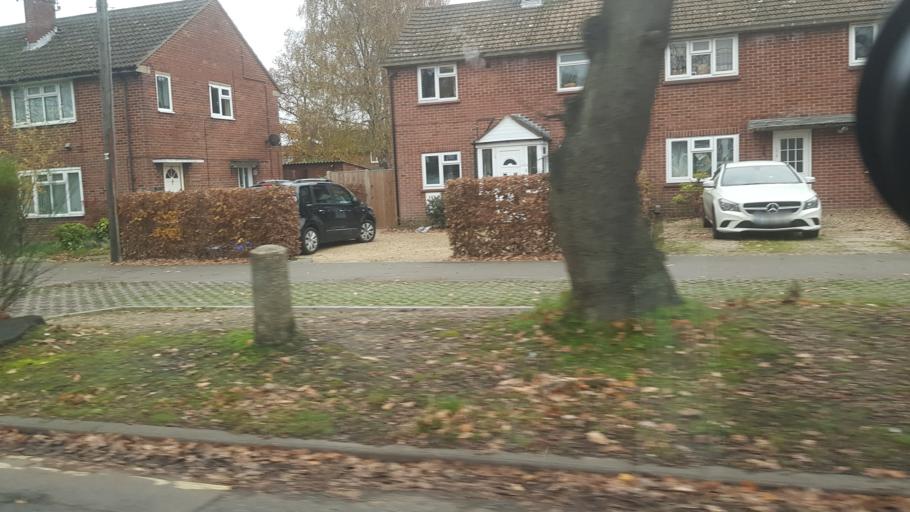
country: GB
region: England
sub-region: Hampshire
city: Farnborough
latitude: 51.3117
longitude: -0.7754
